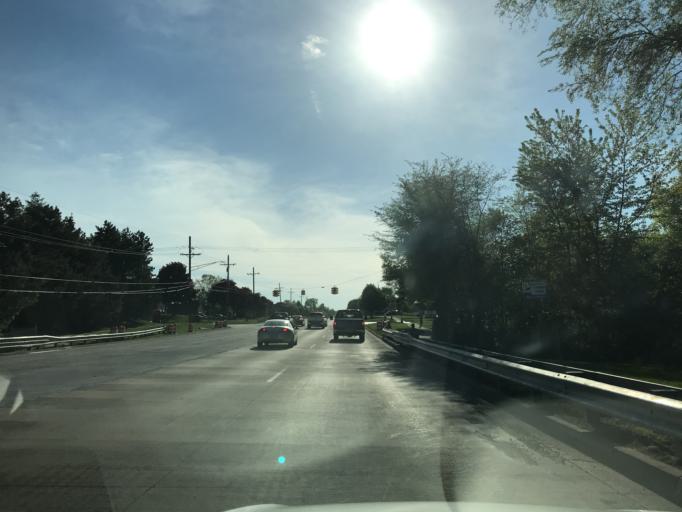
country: US
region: Michigan
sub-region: Oakland County
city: Farmington
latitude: 42.4404
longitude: -83.3839
